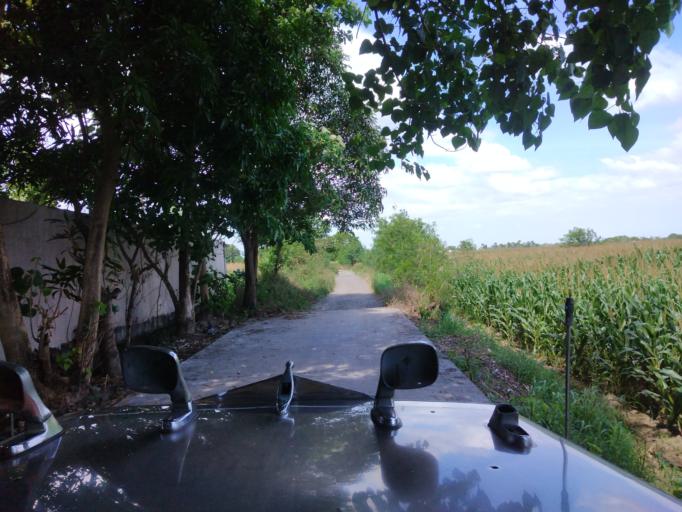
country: PH
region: Central Luzon
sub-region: Province of Pampanga
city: Anao
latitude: 15.1296
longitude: 120.6996
